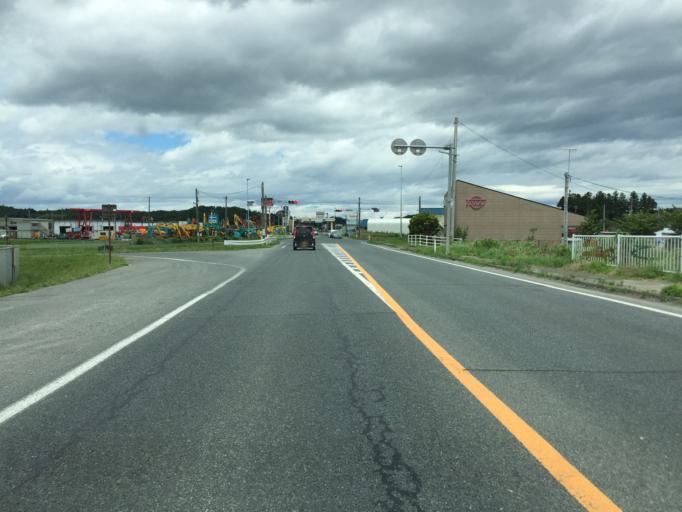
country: JP
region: Fukushima
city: Namie
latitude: 37.6497
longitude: 140.9854
